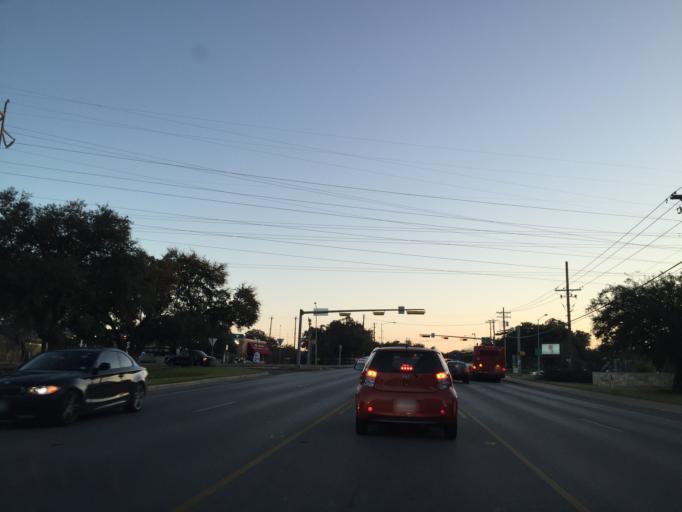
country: US
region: Texas
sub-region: Williamson County
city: Jollyville
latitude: 30.4015
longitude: -97.7487
